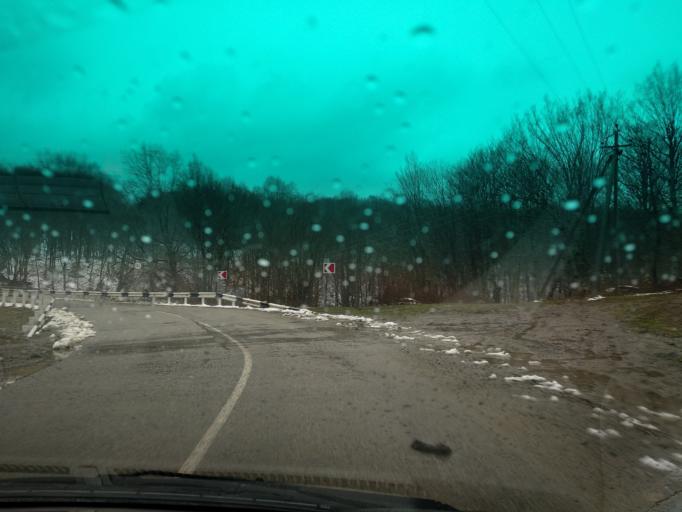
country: RU
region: Krasnodarskiy
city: Khadyzhensk
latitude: 44.2110
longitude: 39.4126
